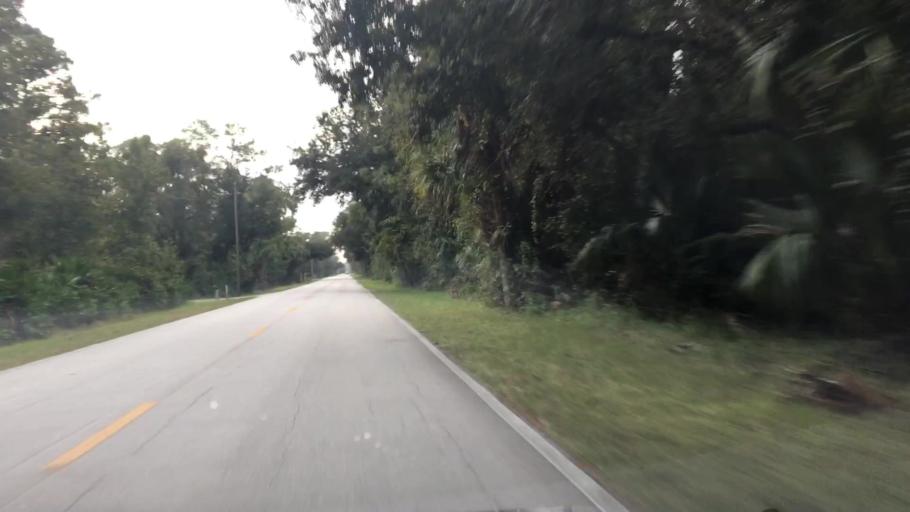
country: US
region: Florida
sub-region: Seminole County
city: Midway
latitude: 28.8464
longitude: -81.2010
